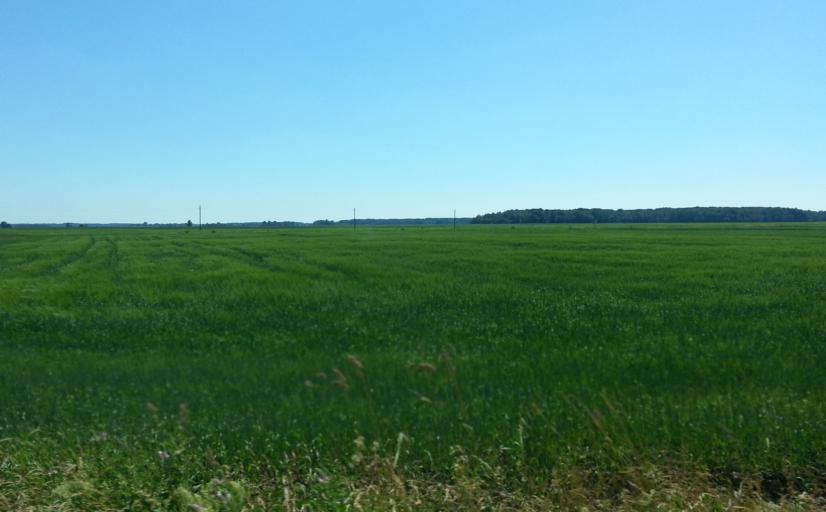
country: LT
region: Panevezys
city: Pasvalys
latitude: 56.2252
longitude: 24.4930
